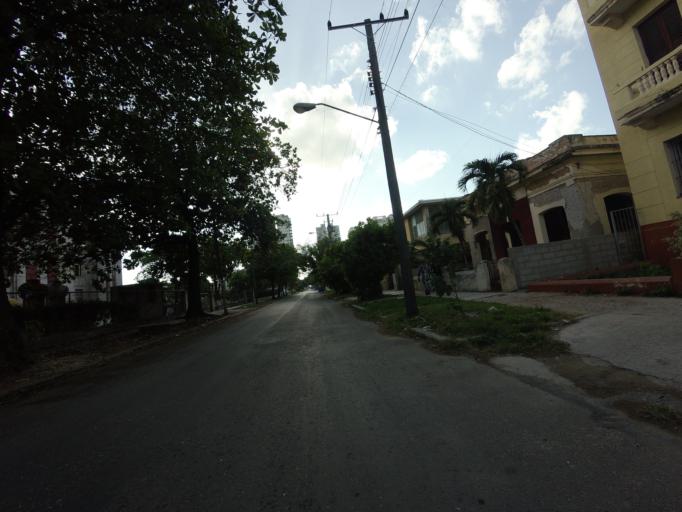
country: CU
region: La Habana
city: Havana
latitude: 23.1427
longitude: -82.3925
